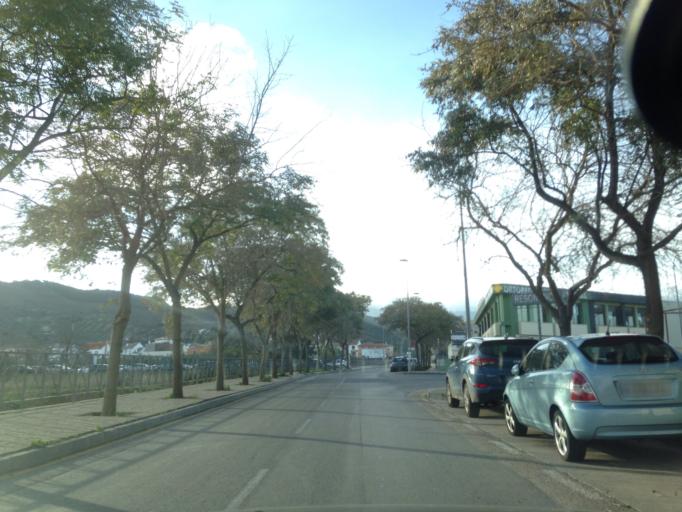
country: ES
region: Andalusia
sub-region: Provincia de Malaga
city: Antequera
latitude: 37.0313
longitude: -4.5303
